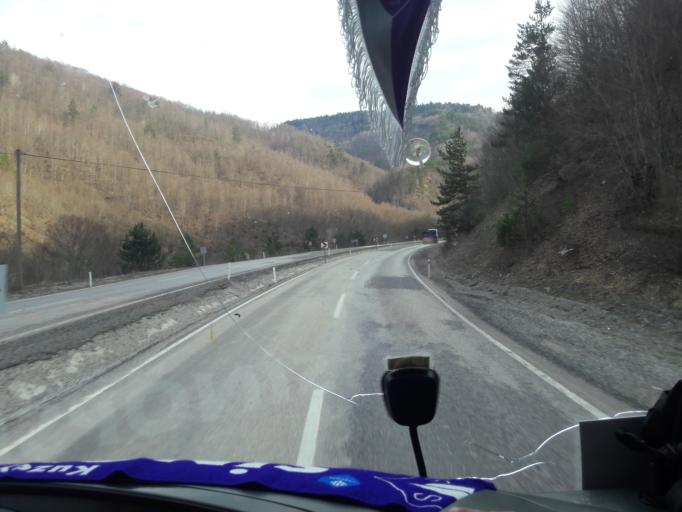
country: TR
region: Kastamonu
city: Kuzyaka
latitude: 41.1390
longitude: 33.7773
